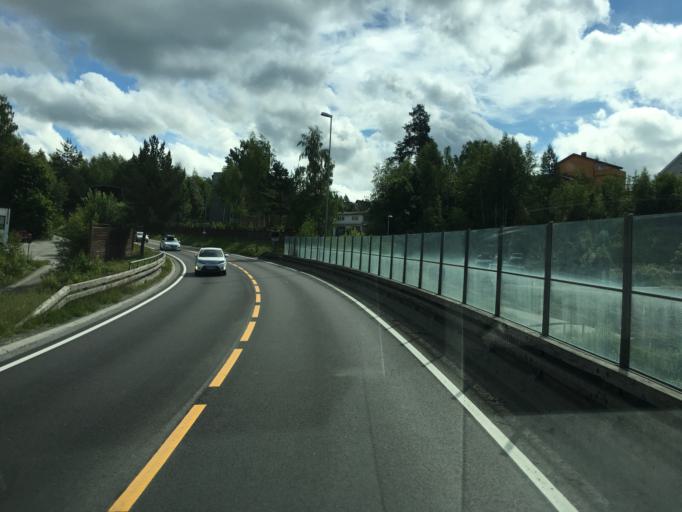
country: NO
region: Oppland
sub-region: Lillehammer
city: Lillehammer
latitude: 61.1151
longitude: 10.4538
